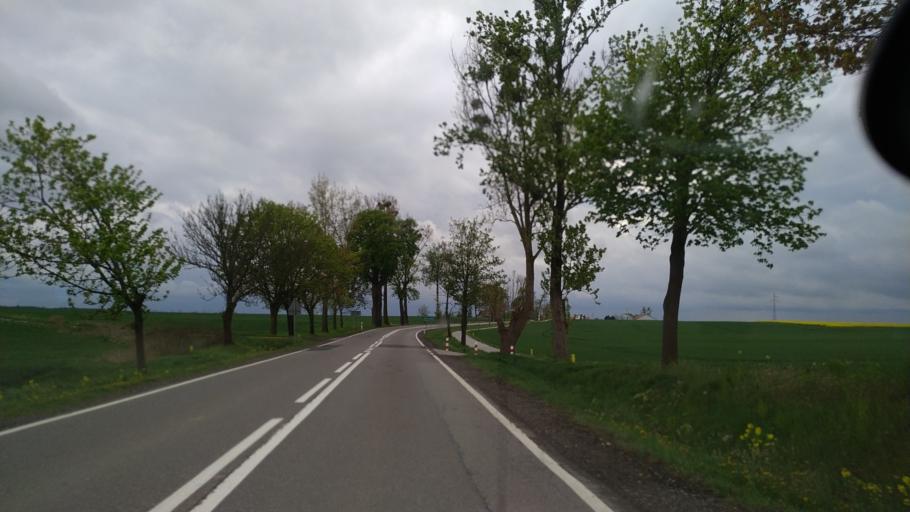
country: PL
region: Pomeranian Voivodeship
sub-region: Powiat kwidzynski
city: Kwidzyn
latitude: 53.7779
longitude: 18.9569
